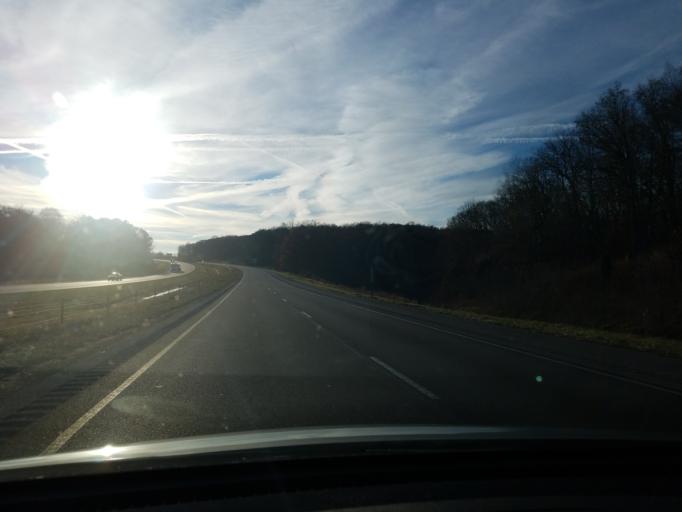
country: US
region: Indiana
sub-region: Crawford County
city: English
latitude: 38.2344
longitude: -86.5600
